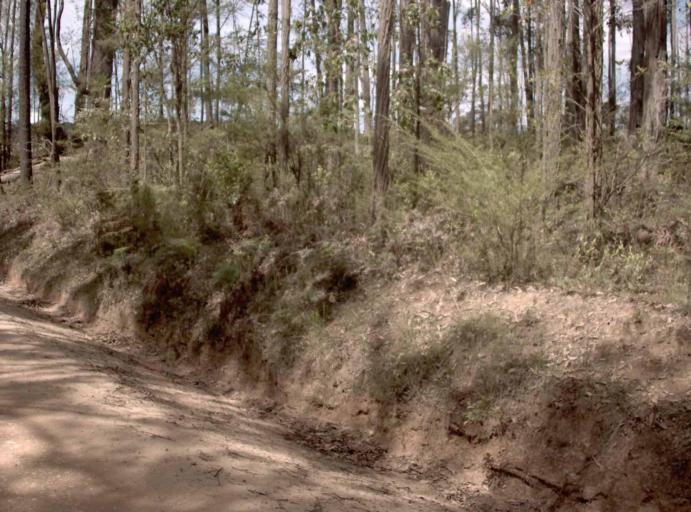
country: AU
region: Victoria
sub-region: East Gippsland
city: Lakes Entrance
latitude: -37.6428
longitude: 148.6622
